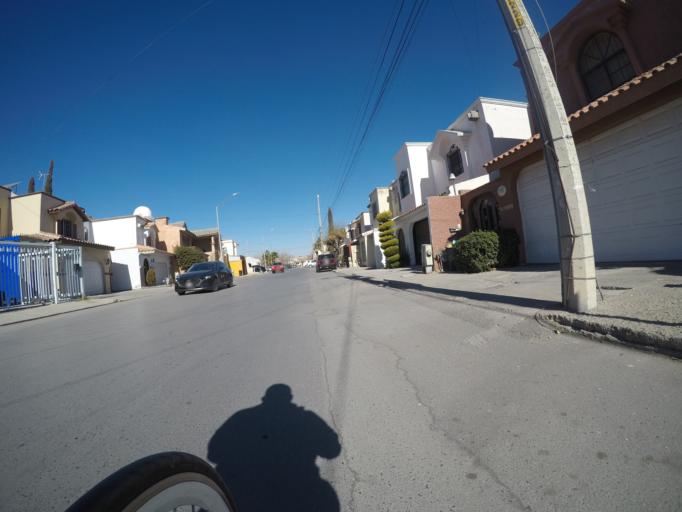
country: MX
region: Chihuahua
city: Ciudad Juarez
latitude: 31.7041
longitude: -106.4132
